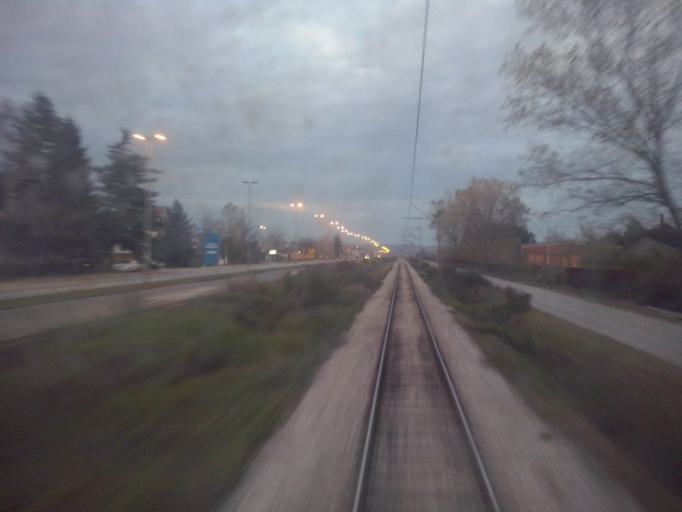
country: RS
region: Central Serbia
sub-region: Kolubarski Okrug
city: Valjevo
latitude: 44.2851
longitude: 19.9394
